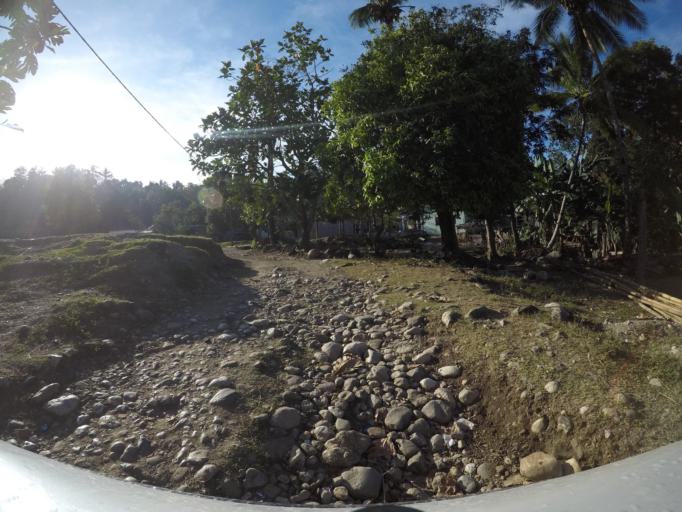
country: TL
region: Viqueque
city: Viqueque
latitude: -8.8318
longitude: 126.3734
